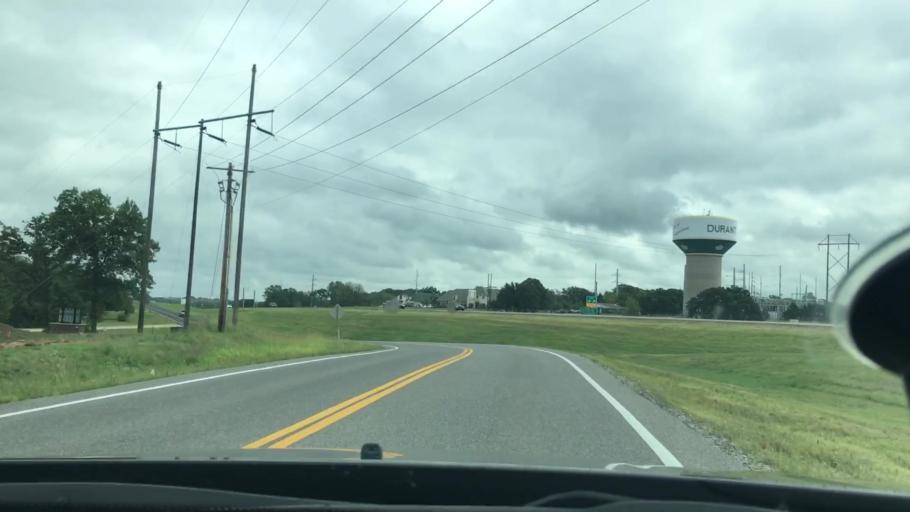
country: US
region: Oklahoma
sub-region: Bryan County
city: Durant
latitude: 34.0070
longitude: -96.3994
